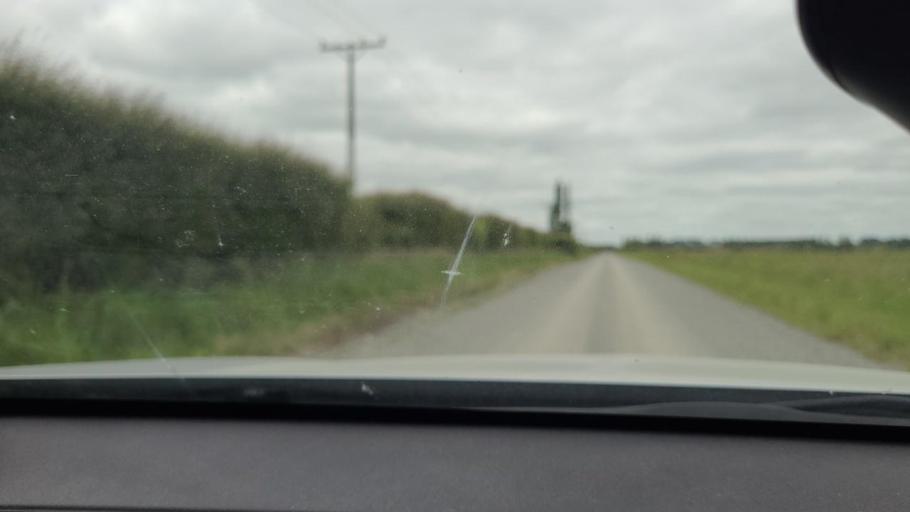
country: NZ
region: Southland
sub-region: Southland District
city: Riverton
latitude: -46.0787
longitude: 168.0574
